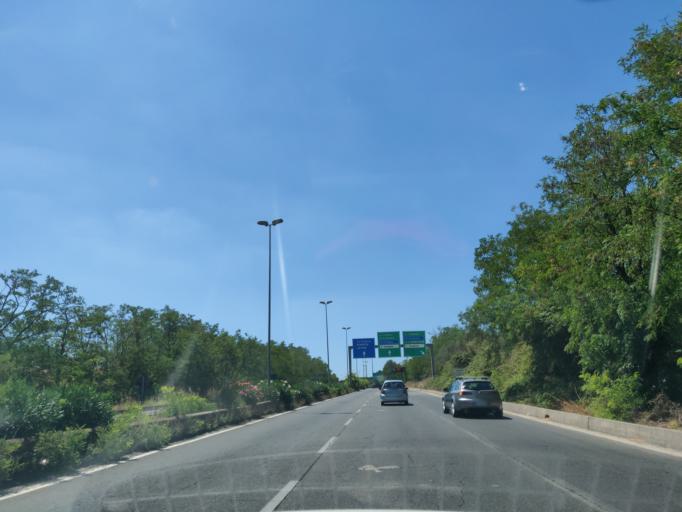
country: IT
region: Latium
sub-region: Citta metropolitana di Roma Capitale
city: Selcetta
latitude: 41.8059
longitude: 12.4556
